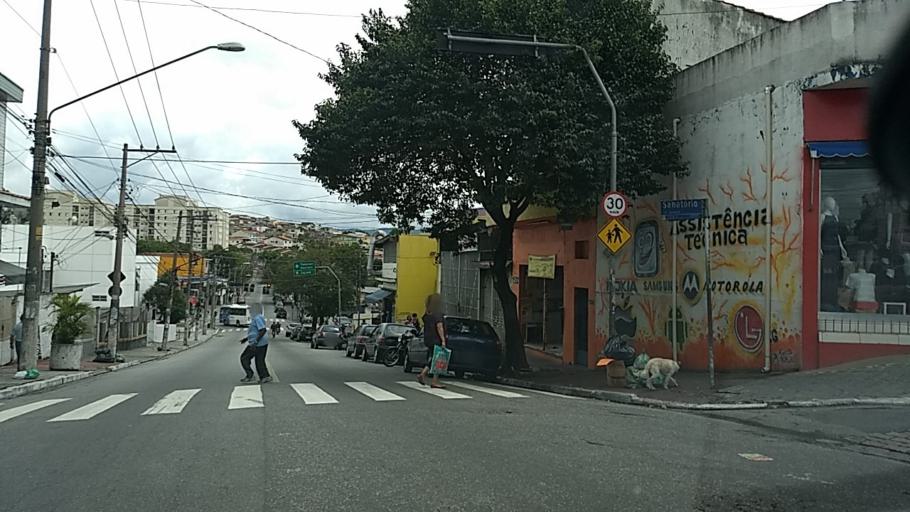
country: BR
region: Sao Paulo
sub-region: Guarulhos
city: Guarulhos
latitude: -23.4793
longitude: -46.5822
